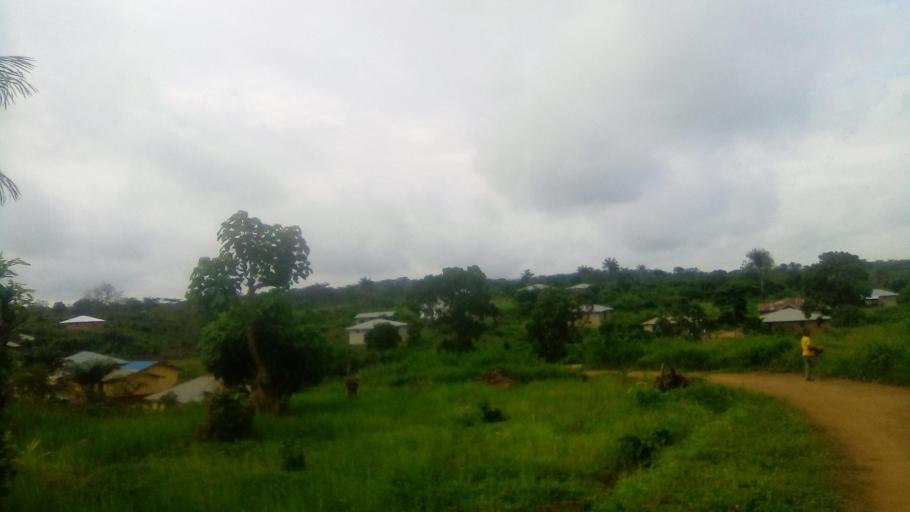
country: SL
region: Eastern Province
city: Kailahun
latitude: 8.2704
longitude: -10.5692
